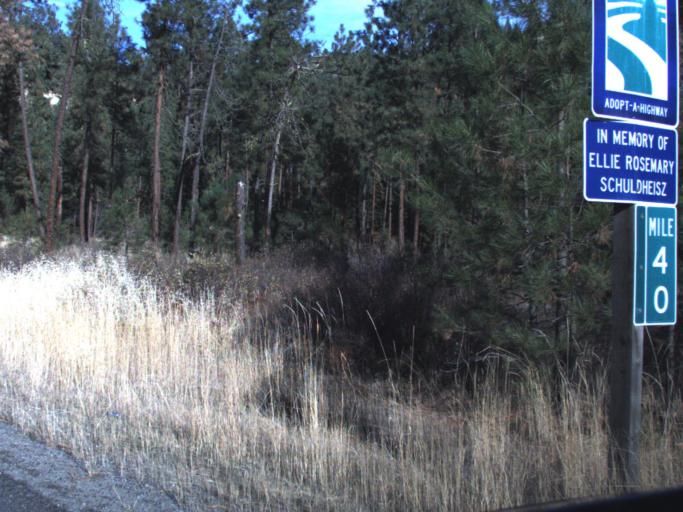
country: US
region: Washington
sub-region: Lincoln County
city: Davenport
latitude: 48.0975
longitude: -118.2013
